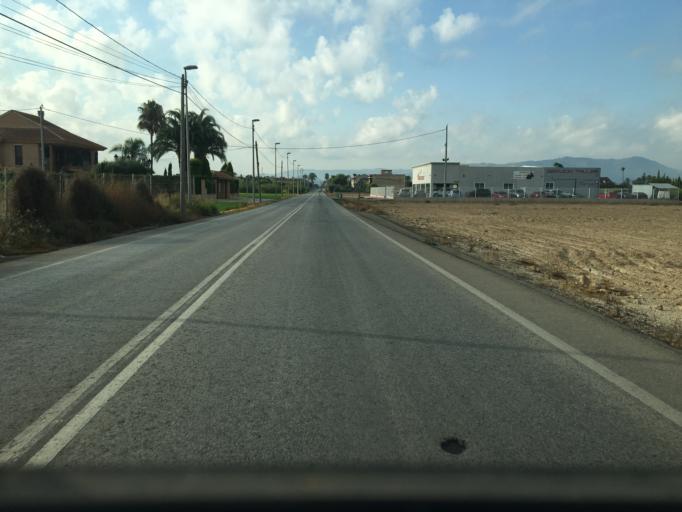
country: ES
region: Murcia
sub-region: Murcia
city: Santomera
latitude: 38.0377
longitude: -1.0458
